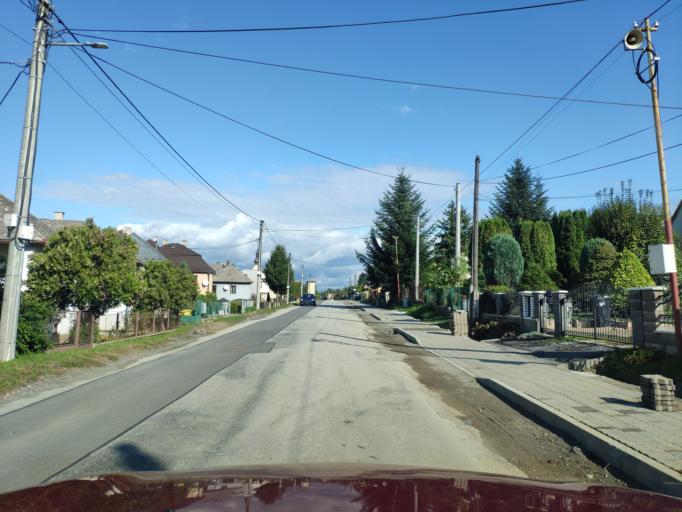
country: SK
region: Presovsky
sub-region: Okres Presov
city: Presov
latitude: 48.9148
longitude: 21.2603
